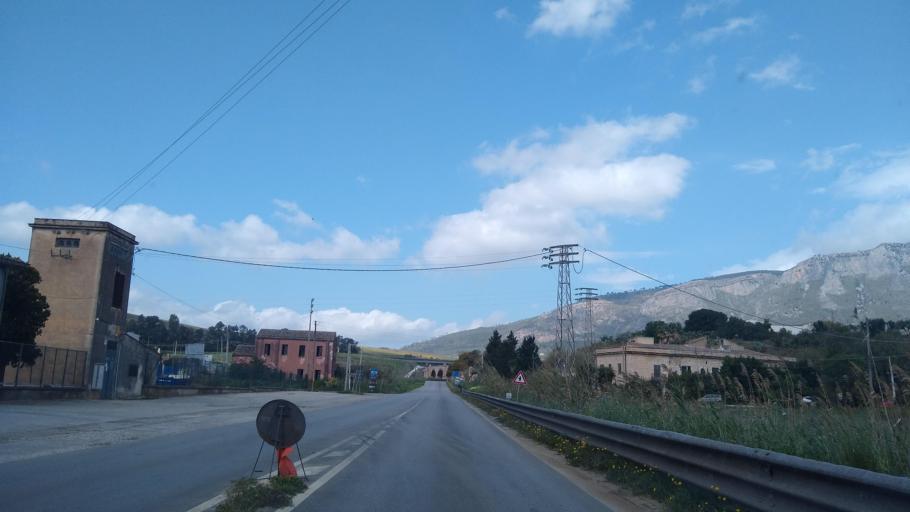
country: IT
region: Sicily
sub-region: Trapani
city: Alcamo
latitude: 37.9678
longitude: 12.9141
